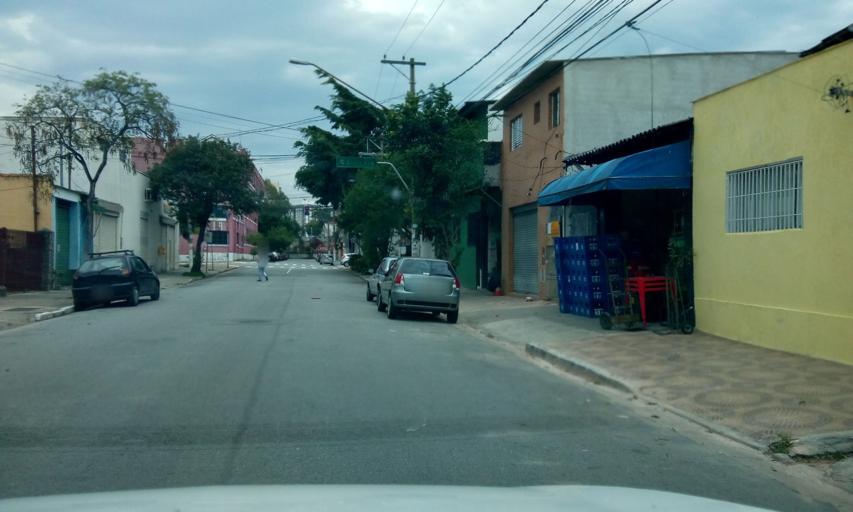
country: BR
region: Sao Paulo
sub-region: Sao Paulo
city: Sao Paulo
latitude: -23.5154
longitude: -46.7044
